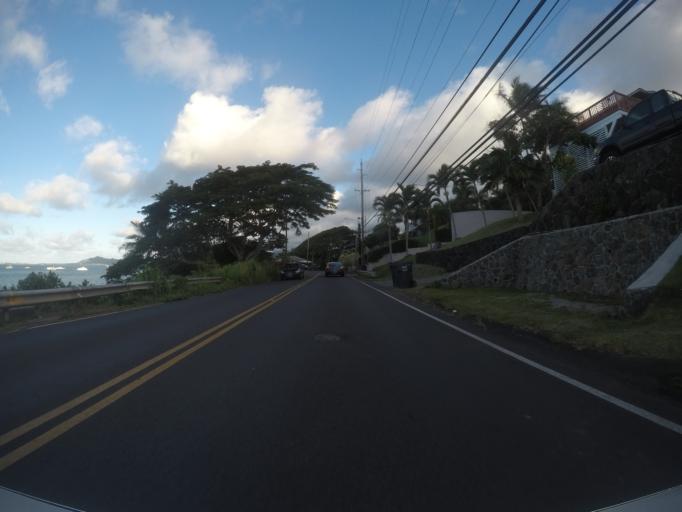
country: US
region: Hawaii
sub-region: Honolulu County
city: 'Ahuimanu
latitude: 21.4512
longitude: -157.8150
